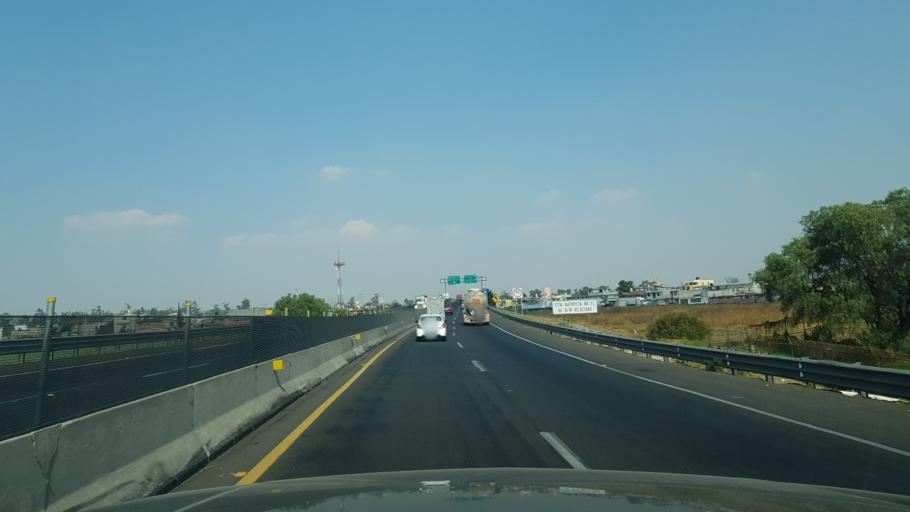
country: MX
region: Mexico
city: Santiago Teyahualco
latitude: 19.6552
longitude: -99.1463
